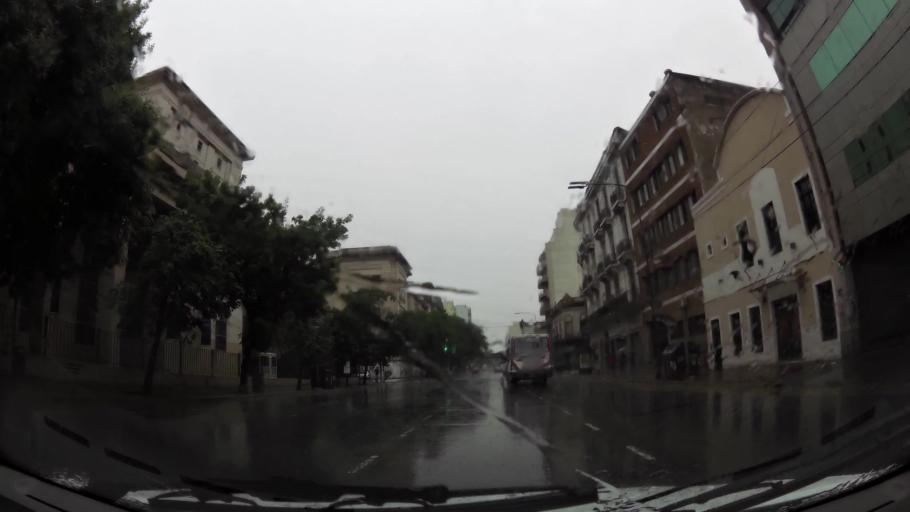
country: AR
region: Buenos Aires F.D.
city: Buenos Aires
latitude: -34.6257
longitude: -58.3913
